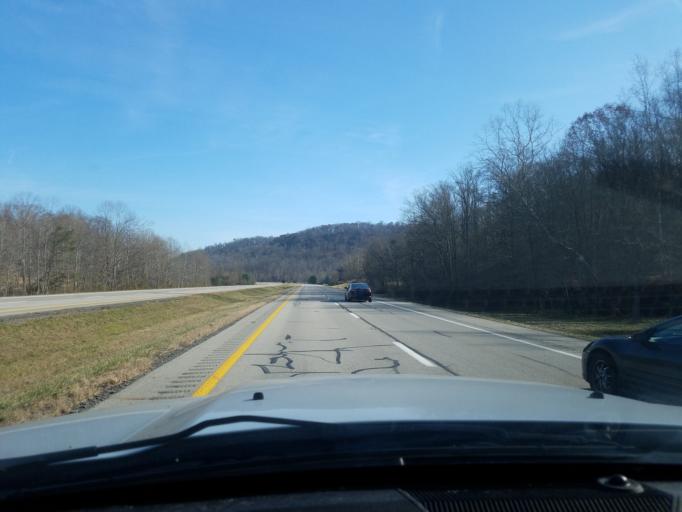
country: US
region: Ohio
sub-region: Adams County
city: Peebles
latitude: 39.0375
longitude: -83.2533
